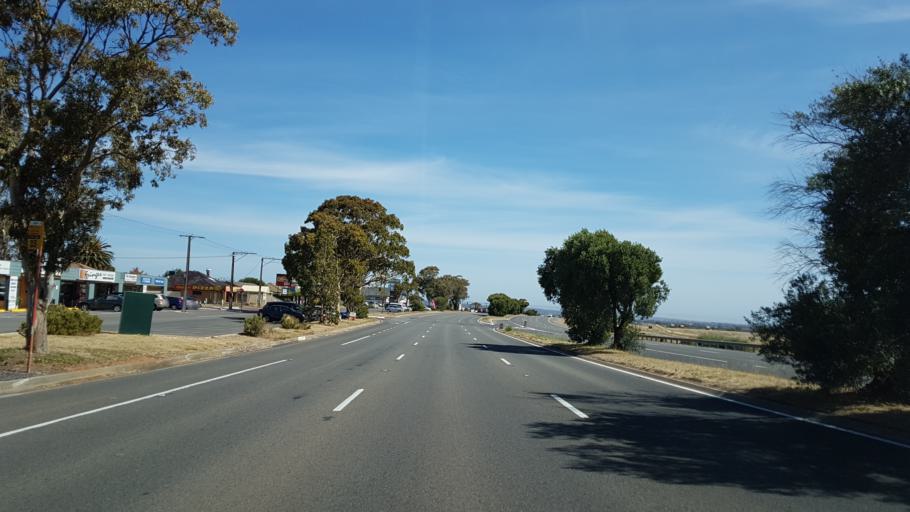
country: AU
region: South Australia
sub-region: Marion
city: Trott Park
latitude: -35.0654
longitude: 138.5550
